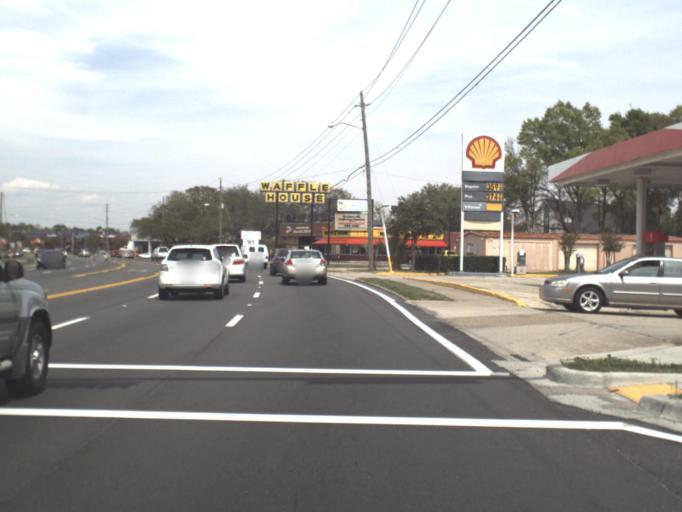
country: US
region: Florida
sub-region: Okaloosa County
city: Lake Lorraine
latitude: 30.4395
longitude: -86.5835
